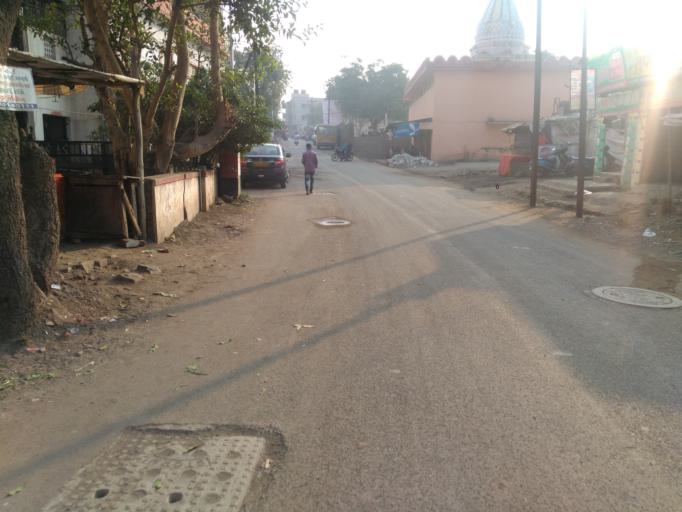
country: IN
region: Maharashtra
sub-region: Pune Division
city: Pune
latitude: 18.4354
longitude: 73.8916
